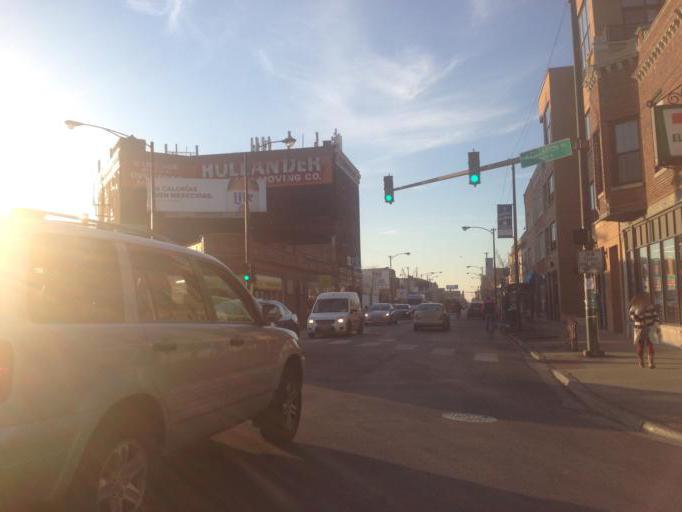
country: US
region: Illinois
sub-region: Cook County
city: Lincolnwood
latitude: 41.9248
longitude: -87.7003
